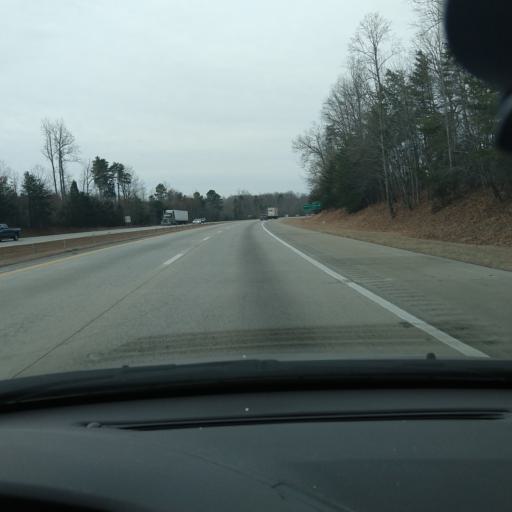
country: US
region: North Carolina
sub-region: Forsyth County
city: Kernersville
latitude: 36.0780
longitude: -80.0958
